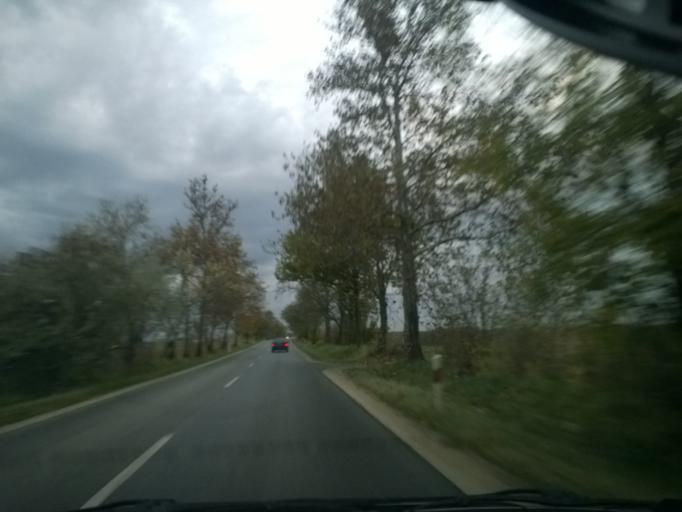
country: HU
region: Bacs-Kiskun
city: Tass
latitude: 47.0551
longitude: 19.0198
